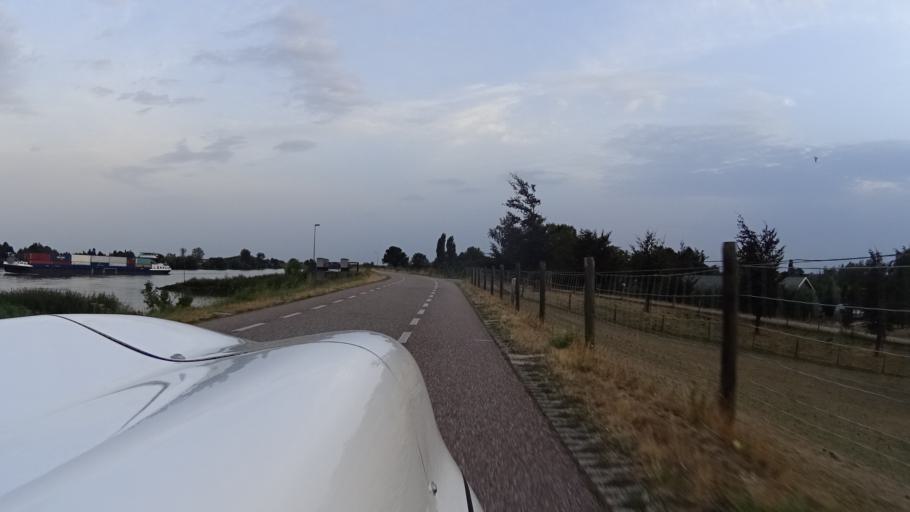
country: NL
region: Utrecht
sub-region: Gemeente Lopik
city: Lopik
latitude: 51.9605
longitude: 4.9309
